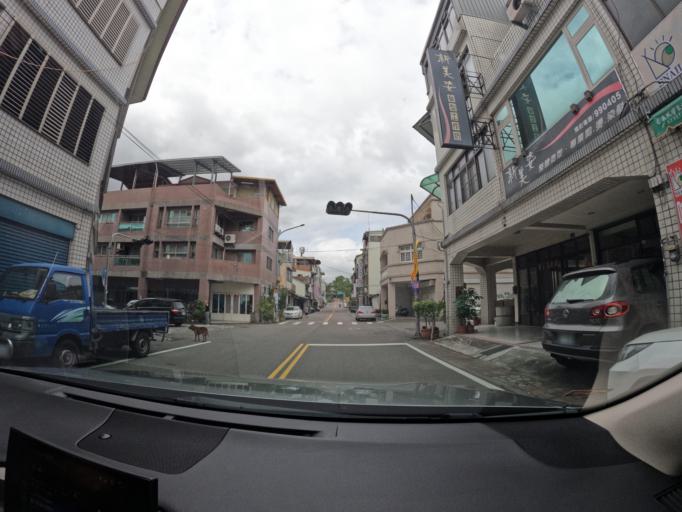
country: TW
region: Taiwan
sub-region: Miaoli
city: Miaoli
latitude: 24.4248
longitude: 120.8701
